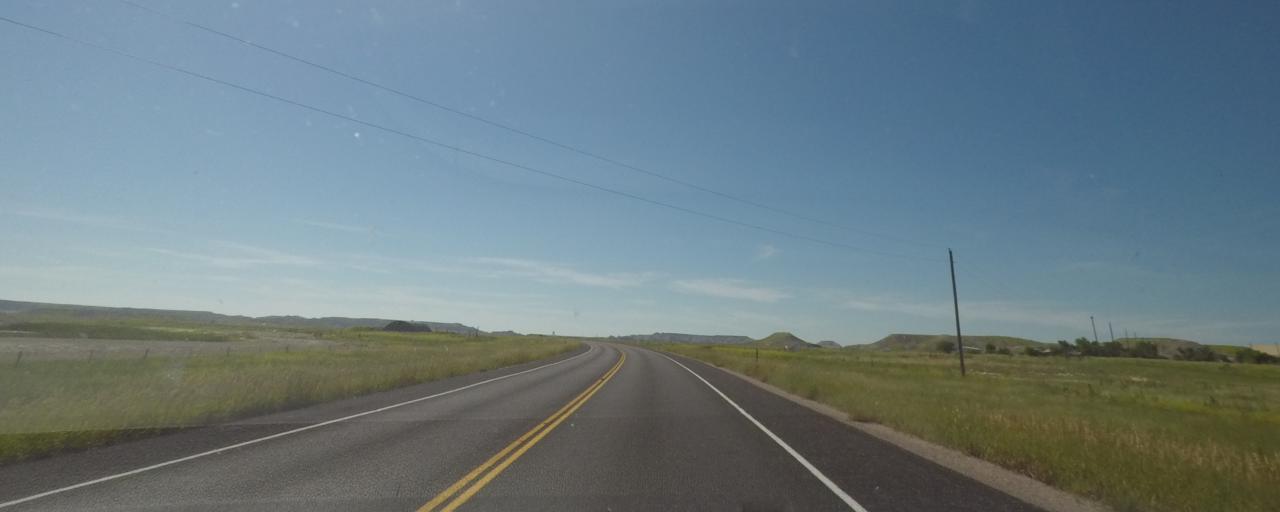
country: US
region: South Dakota
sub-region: Shannon County
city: Porcupine
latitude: 43.7823
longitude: -102.5533
